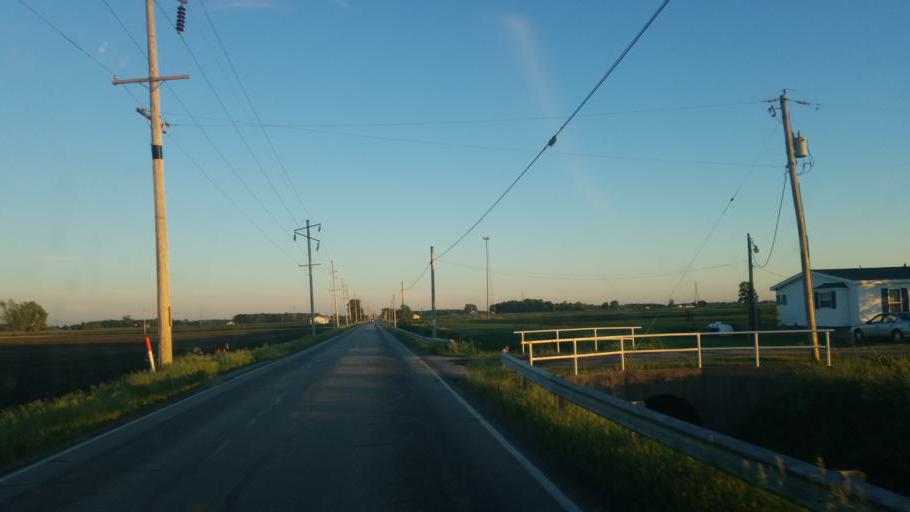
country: US
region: Indiana
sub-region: Elkhart County
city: Nappanee
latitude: 41.4172
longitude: -86.0012
